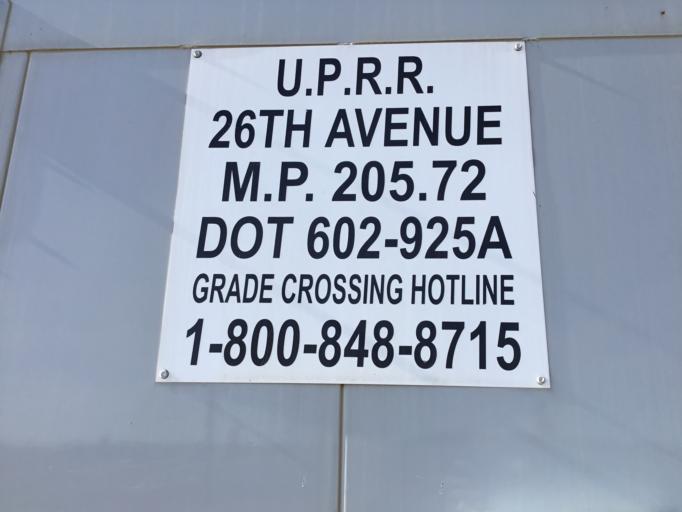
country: US
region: Kansas
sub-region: McPherson County
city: Moundridge
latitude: 38.3845
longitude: -97.4457
